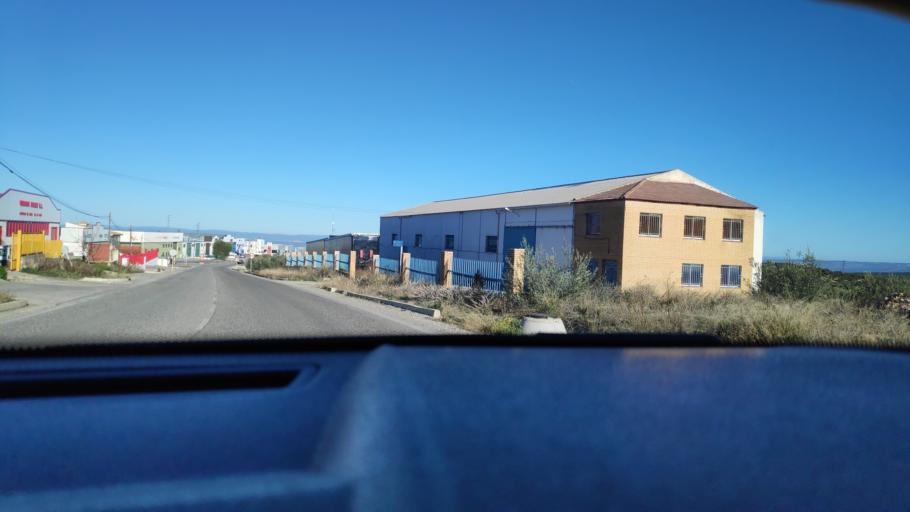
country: ES
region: Andalusia
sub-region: Provincia de Jaen
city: Mancha Real
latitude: 37.7966
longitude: -3.6081
